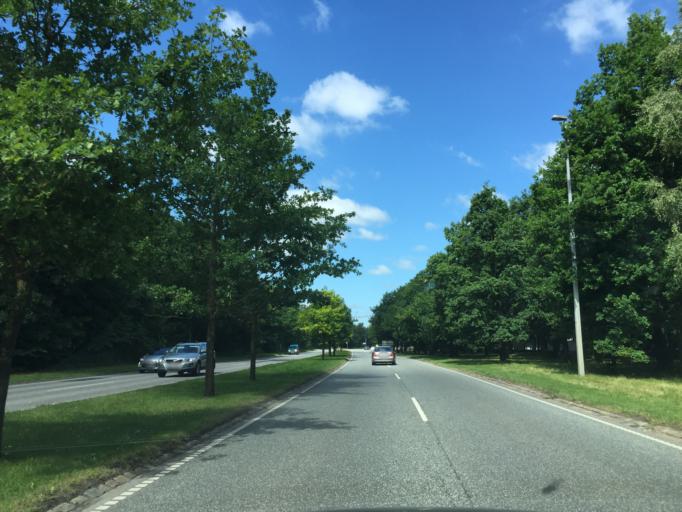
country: DK
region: South Denmark
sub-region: Odense Kommune
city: Neder Holluf
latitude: 55.3747
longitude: 10.4398
